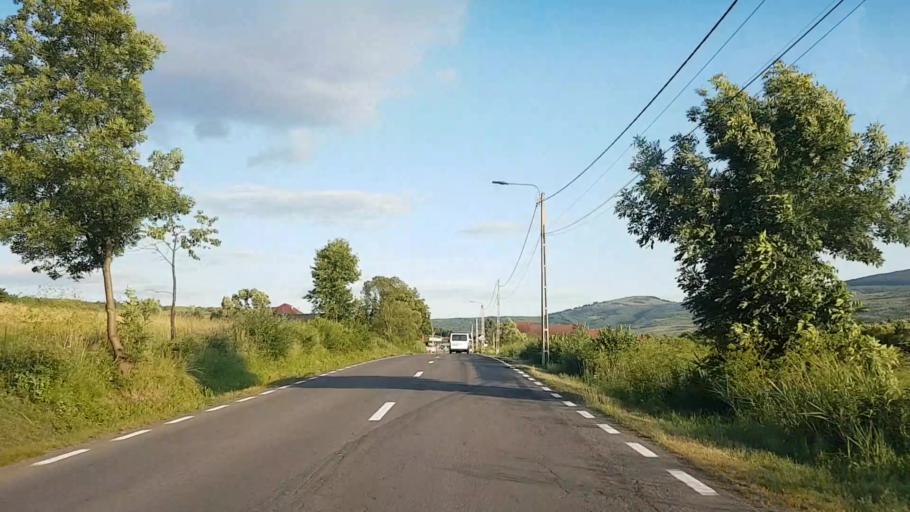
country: RO
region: Harghita
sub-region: Comuna Corund
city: Corund
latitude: 46.4958
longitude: 25.1671
